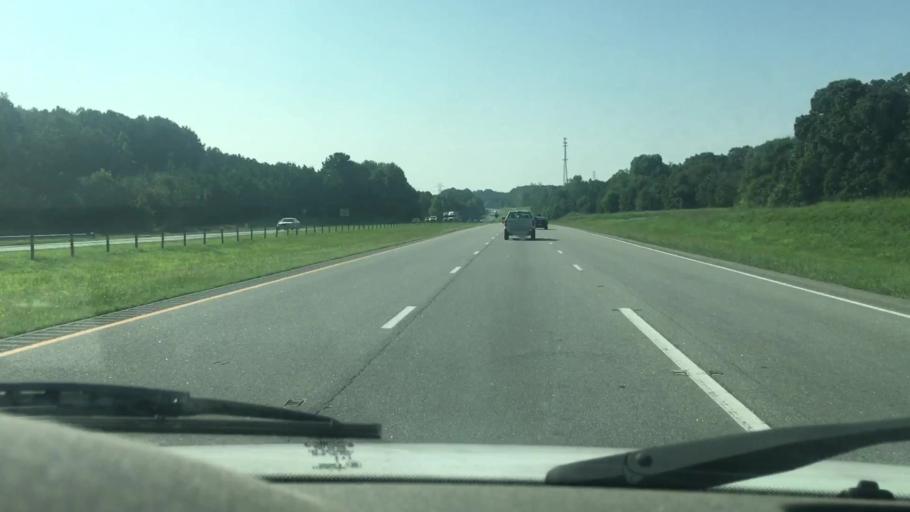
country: US
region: North Carolina
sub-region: Lincoln County
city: Lowesville
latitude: 35.3790
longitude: -80.9996
